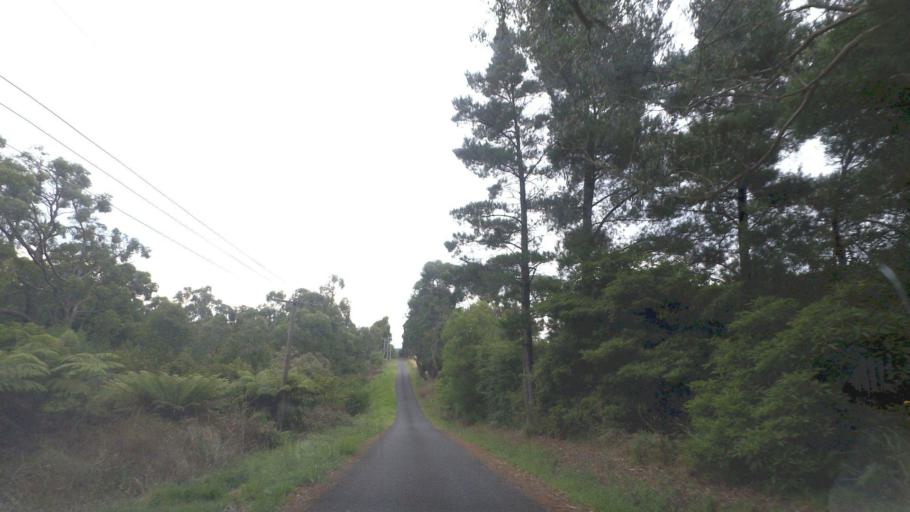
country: AU
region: Victoria
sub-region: Yarra Ranges
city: Mount Evelyn
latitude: -37.7677
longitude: 145.4005
